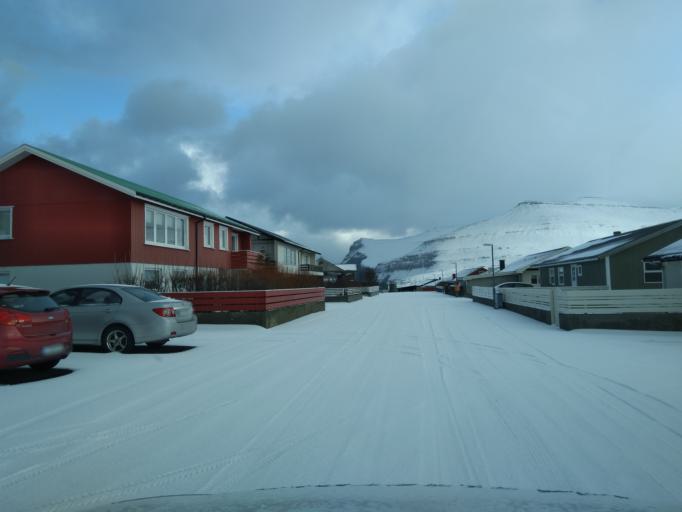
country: FO
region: Eysturoy
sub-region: Eidi
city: Eidi
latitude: 62.3011
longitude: -7.0998
